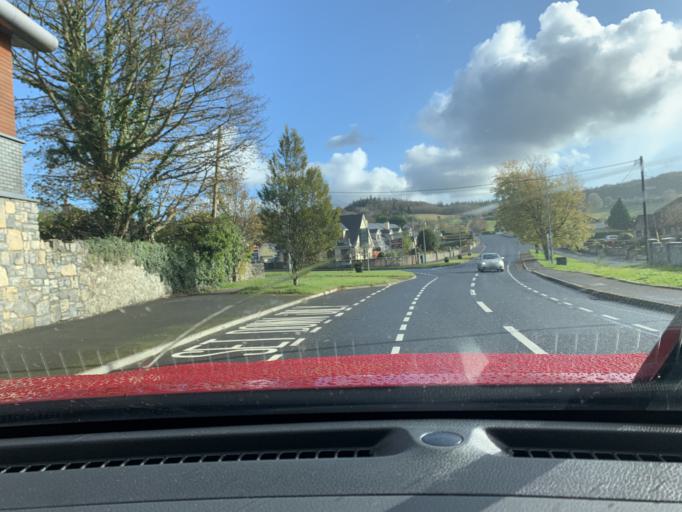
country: IE
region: Connaught
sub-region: Sligo
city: Sligo
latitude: 54.2613
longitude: -8.4610
